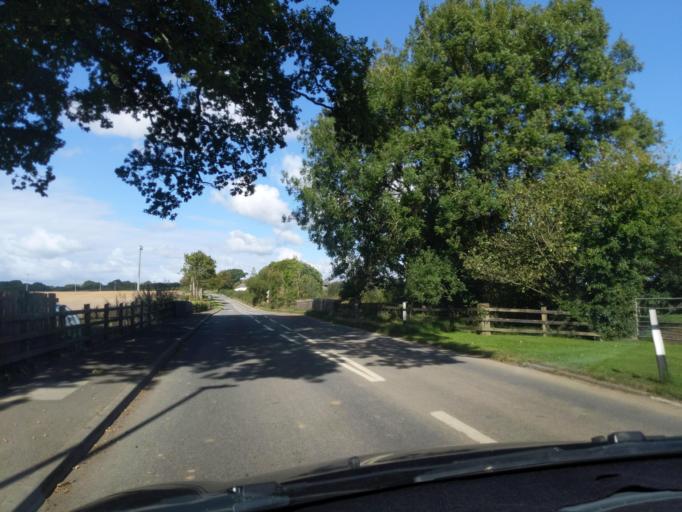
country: GB
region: England
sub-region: Devon
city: Holsworthy
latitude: 50.7699
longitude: -4.3371
